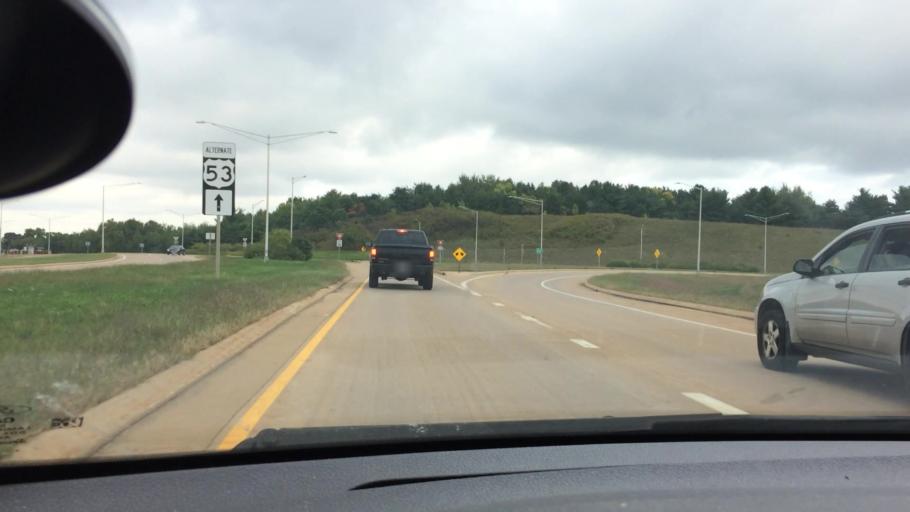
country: US
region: Wisconsin
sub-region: Chippewa County
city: Chippewa Falls
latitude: 44.9199
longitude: -91.3810
